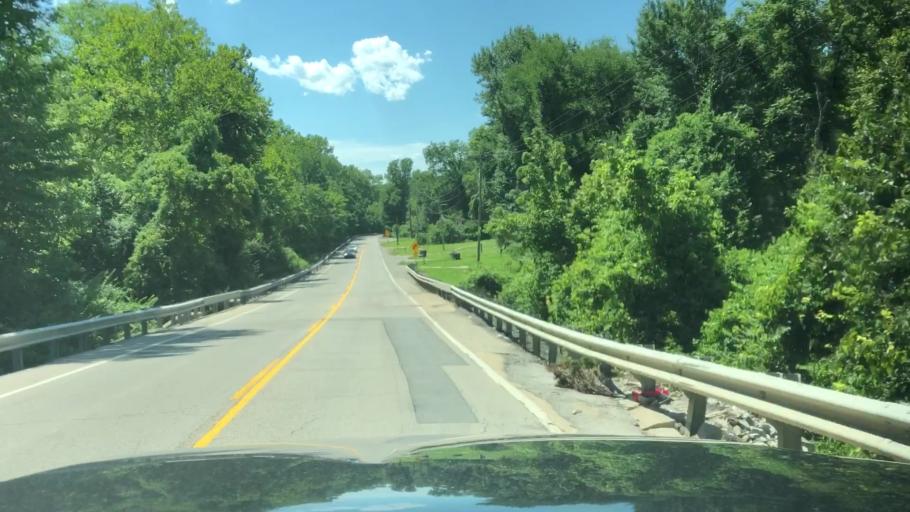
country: US
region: Illinois
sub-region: Saint Clair County
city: Centreville
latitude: 38.5539
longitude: -90.0912
